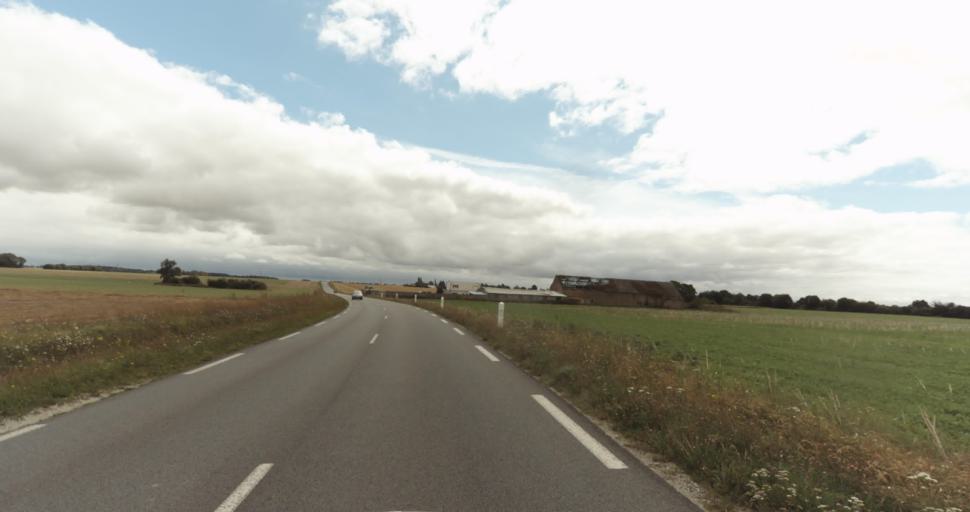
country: FR
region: Haute-Normandie
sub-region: Departement de l'Eure
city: Evreux
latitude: 48.9465
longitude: 1.2247
